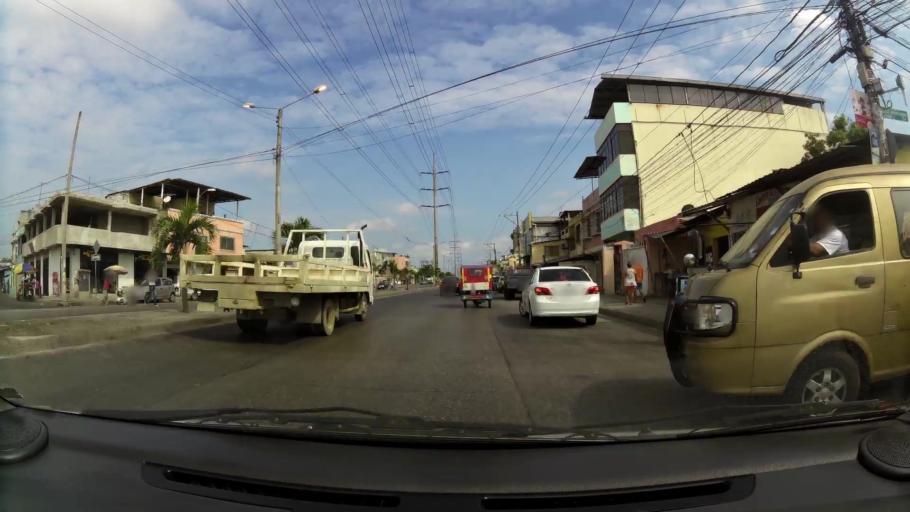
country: EC
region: Guayas
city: Guayaquil
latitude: -2.2593
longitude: -79.8857
